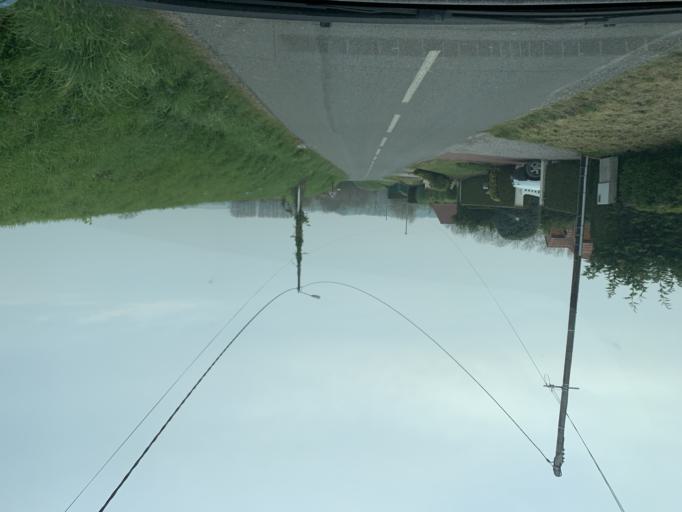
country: FR
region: Nord-Pas-de-Calais
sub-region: Departement du Pas-de-Calais
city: Samer
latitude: 50.6581
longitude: 1.7523
